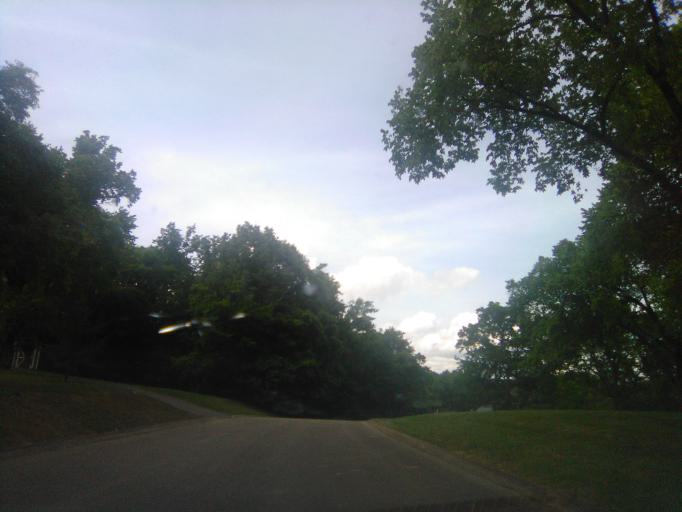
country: US
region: Tennessee
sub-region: Davidson County
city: Belle Meade
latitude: 36.0955
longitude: -86.8888
